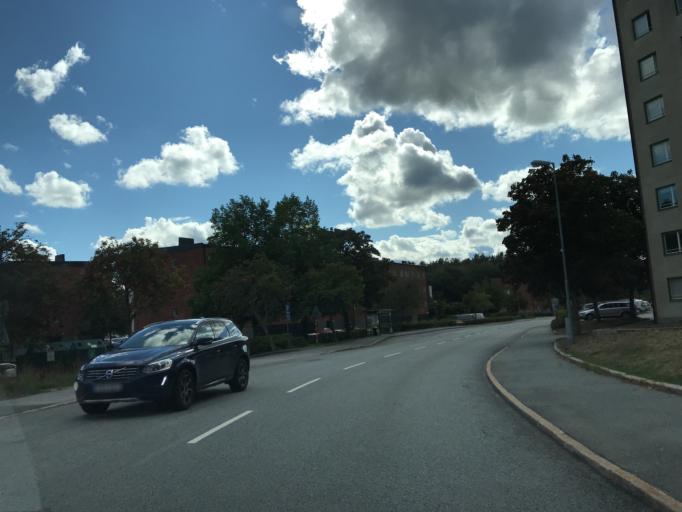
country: SE
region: Stockholm
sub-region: Sollentuna Kommun
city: Sollentuna
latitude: 59.4463
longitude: 17.9757
